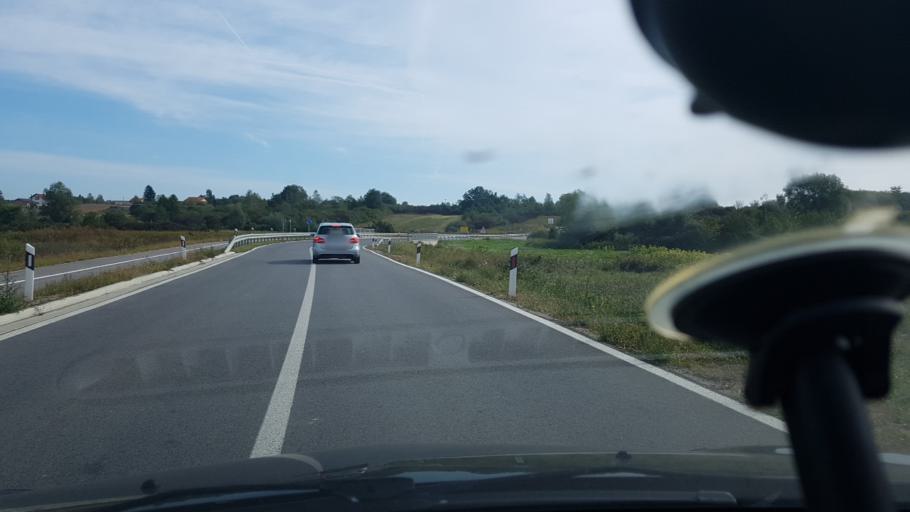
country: HR
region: Krapinsko-Zagorska
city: Marija Bistrica
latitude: 46.0584
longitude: 16.1581
